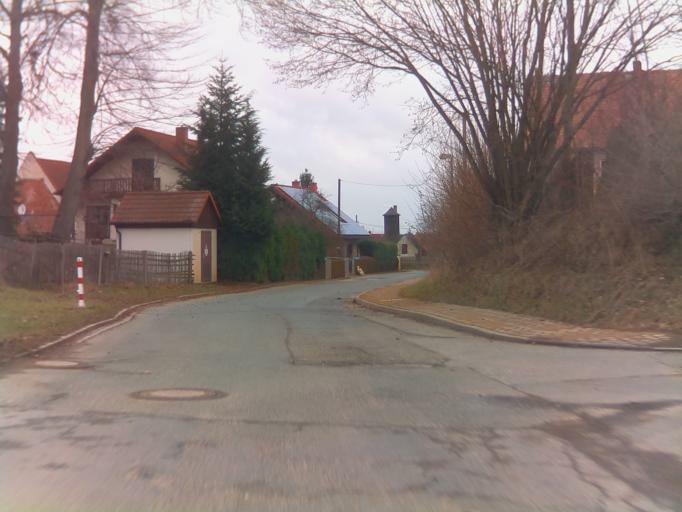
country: DE
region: Thuringia
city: Lemnitz
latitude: 50.7149
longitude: 11.8472
